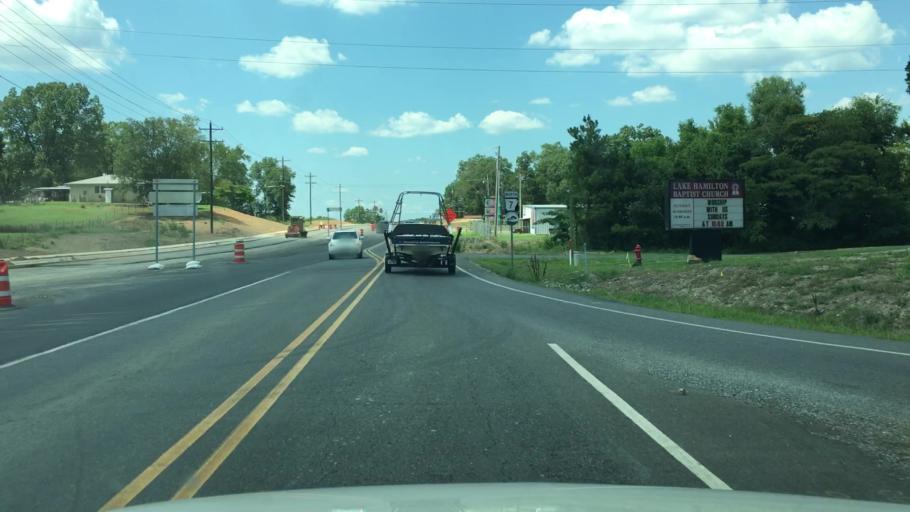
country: US
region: Arkansas
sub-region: Garland County
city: Lake Hamilton
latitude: 34.4129
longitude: -93.0947
